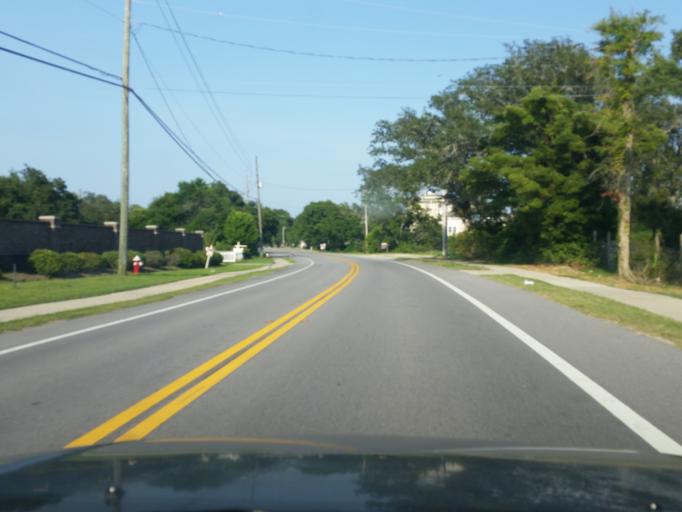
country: US
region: Florida
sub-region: Escambia County
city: Warrington
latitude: 30.3276
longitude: -87.3666
